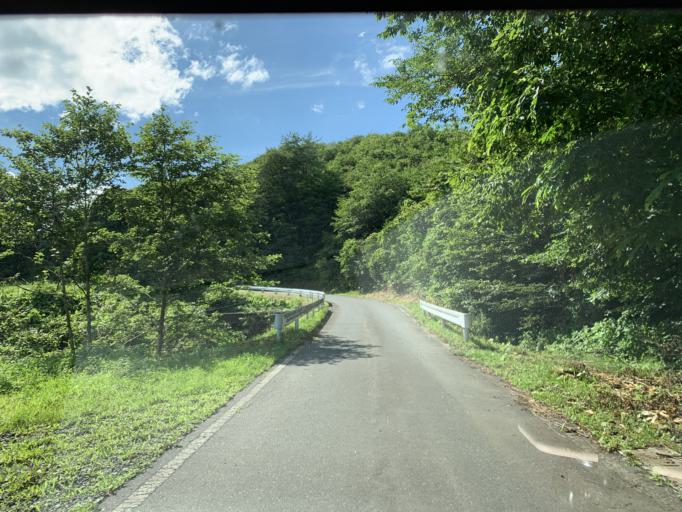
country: JP
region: Iwate
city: Ichinoseki
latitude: 38.9211
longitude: 140.9671
